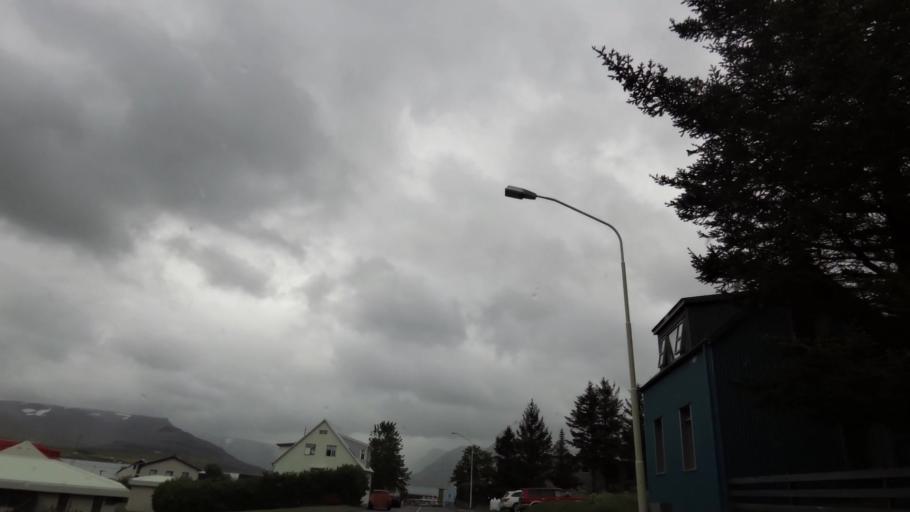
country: IS
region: Westfjords
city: Isafjoerdur
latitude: 65.8780
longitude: -23.4947
